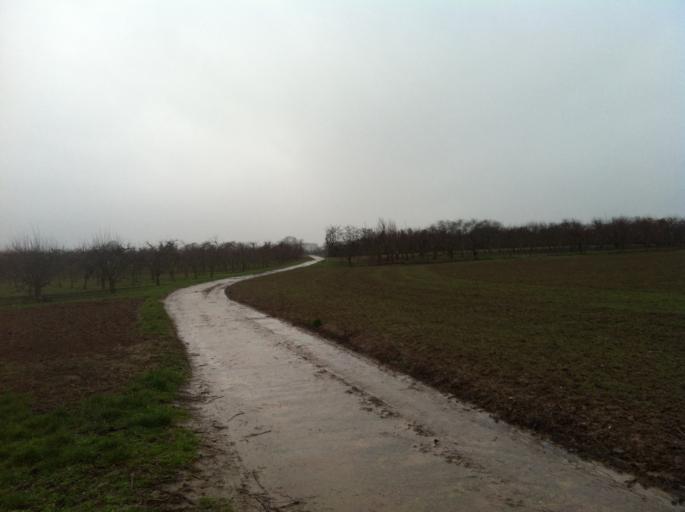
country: DE
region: Rheinland-Pfalz
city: Budenheim
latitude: 49.9921
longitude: 8.1988
